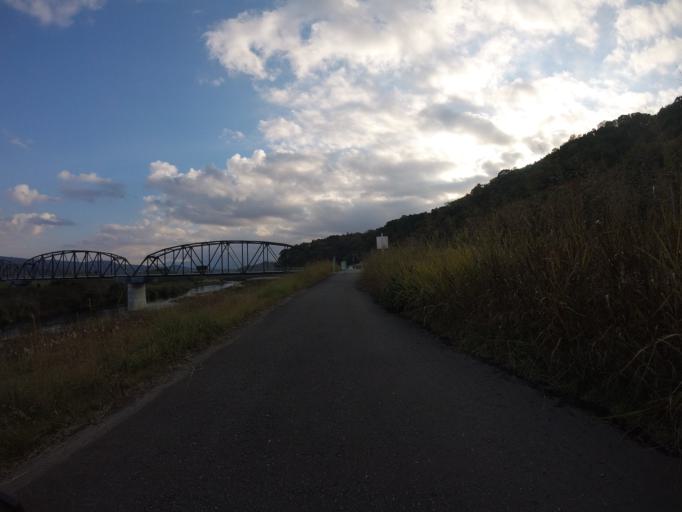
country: JP
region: Shizuoka
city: Mishima
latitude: 35.0658
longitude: 138.9358
